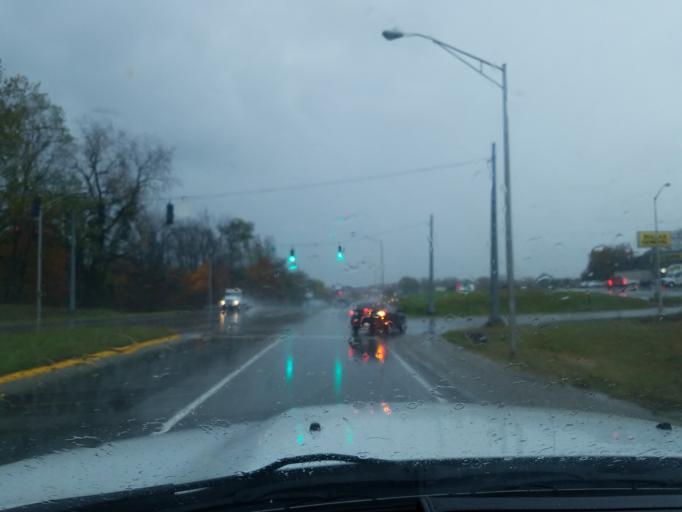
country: US
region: Kentucky
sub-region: Taylor County
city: Campbellsville
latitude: 37.3392
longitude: -85.3561
